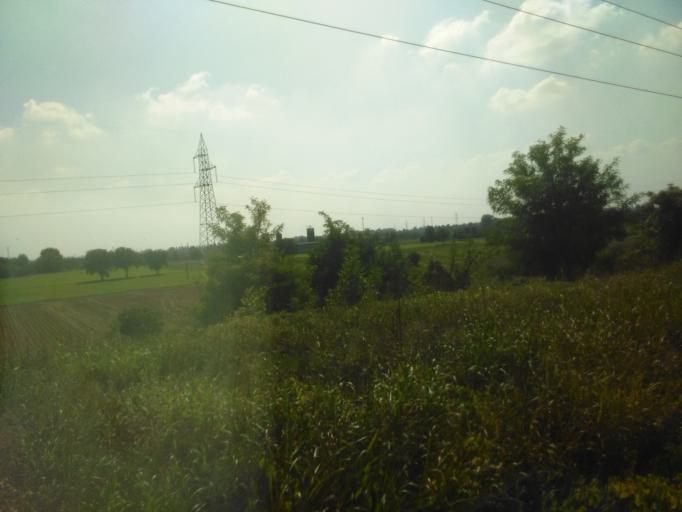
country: IT
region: Lombardy
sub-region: Provincia di Bergamo
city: Casirate d'Adda
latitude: 45.5134
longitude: 9.5626
